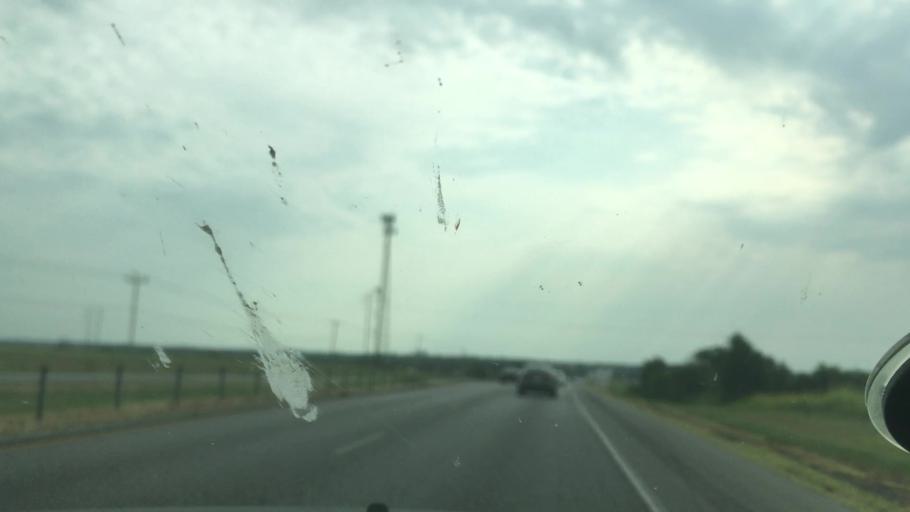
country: US
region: Oklahoma
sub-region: Bryan County
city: Calera
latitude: 33.9110
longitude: -96.4594
